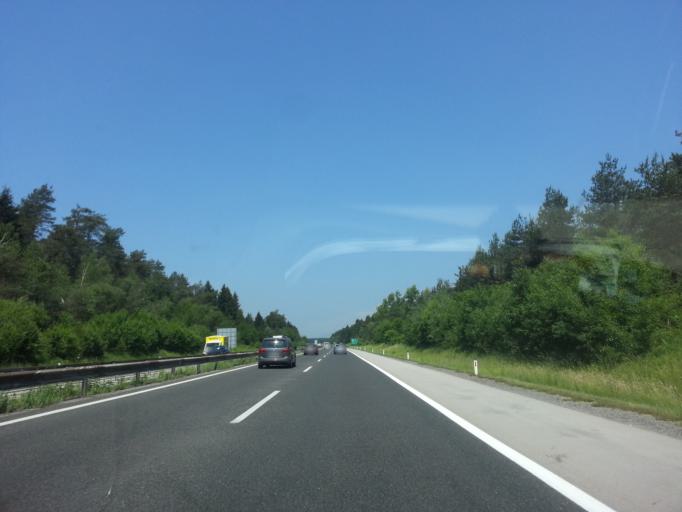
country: SI
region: Vodice
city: Vodice
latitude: 46.2056
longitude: 14.4597
